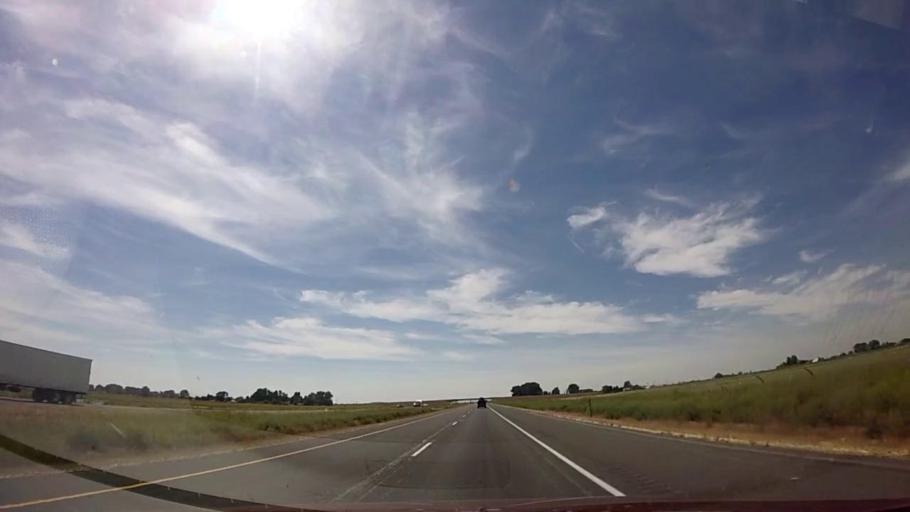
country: US
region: Idaho
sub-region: Minidoka County
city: Rupert
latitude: 42.5689
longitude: -113.6976
